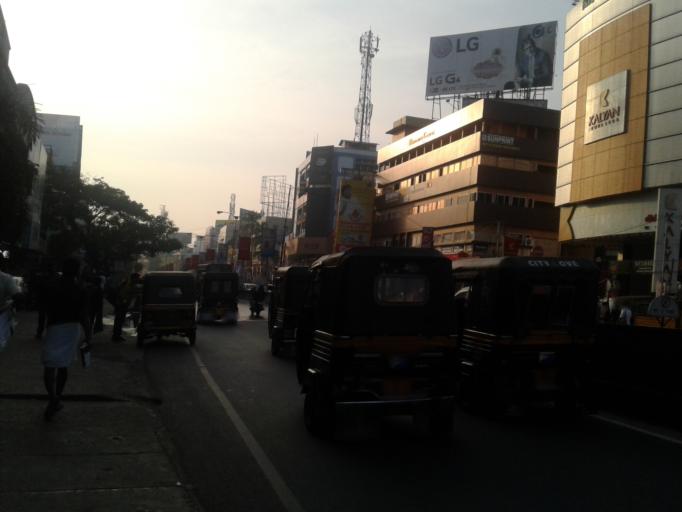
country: IN
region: Kerala
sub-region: Kozhikode
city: Kozhikode
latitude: 11.2592
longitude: 75.7889
